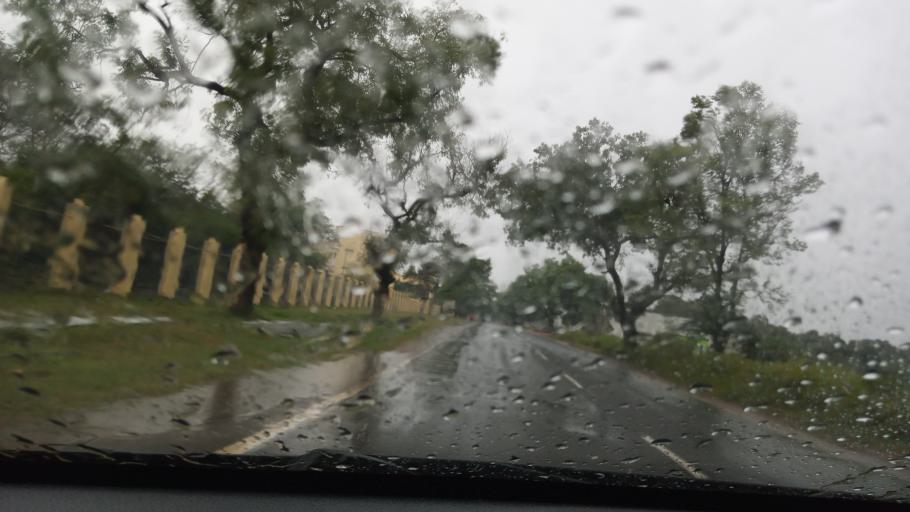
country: IN
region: Tamil Nadu
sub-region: Vellore
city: Kalavai
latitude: 12.8019
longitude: 79.4338
